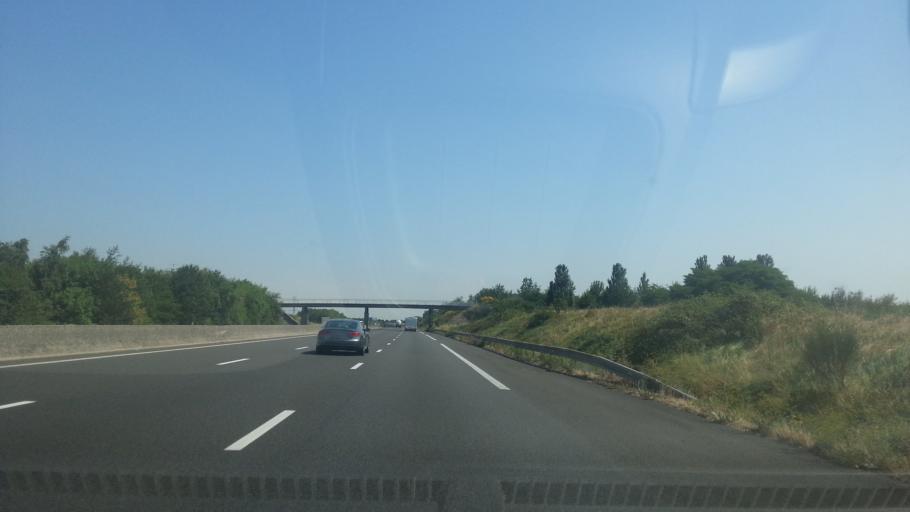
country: FR
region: Centre
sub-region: Departement du Loiret
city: Baule
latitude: 47.8259
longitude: 1.6533
